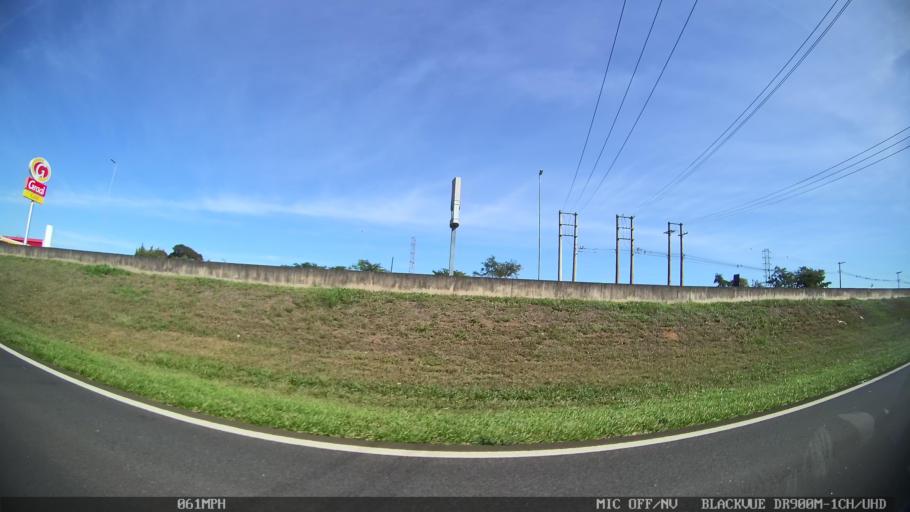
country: BR
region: Sao Paulo
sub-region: Pirassununga
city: Pirassununga
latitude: -22.0007
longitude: -47.4448
